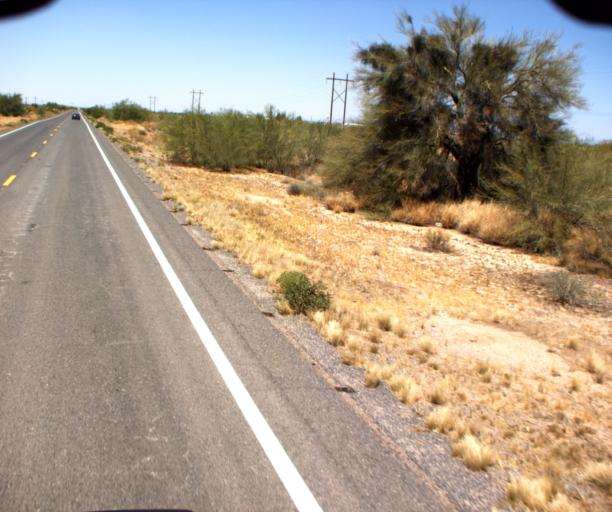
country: US
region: Arizona
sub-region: Pinal County
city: Florence
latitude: 32.9188
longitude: -111.2958
